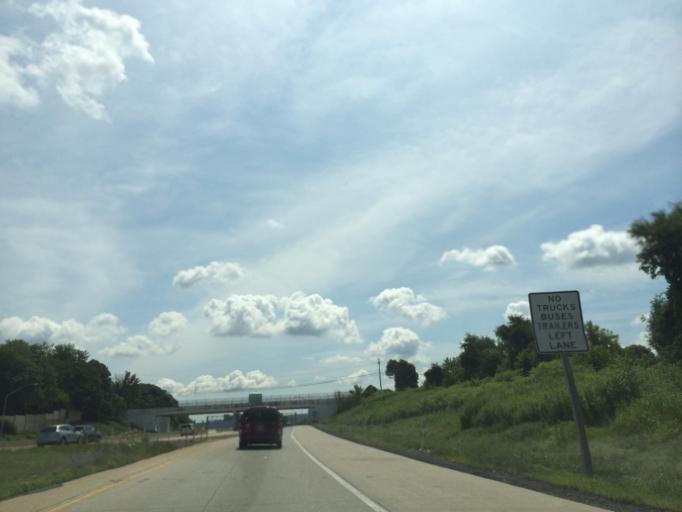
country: US
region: Pennsylvania
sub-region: Lehigh County
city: Wescosville
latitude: 40.5707
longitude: -75.5370
